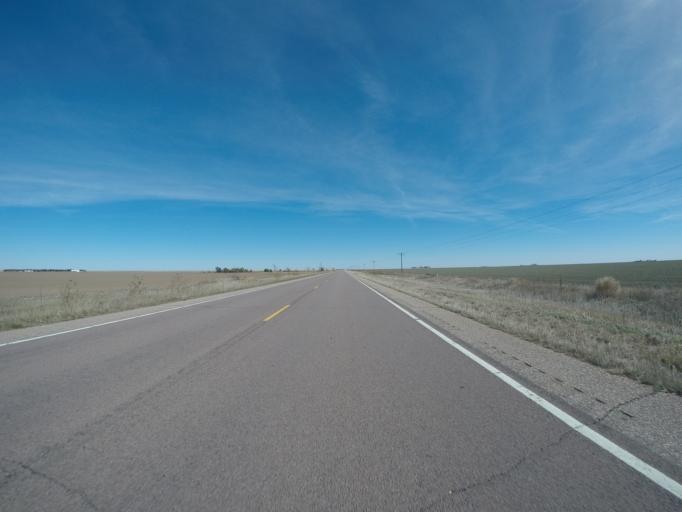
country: US
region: Colorado
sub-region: Kit Carson County
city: Burlington
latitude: 39.6576
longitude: -102.4582
